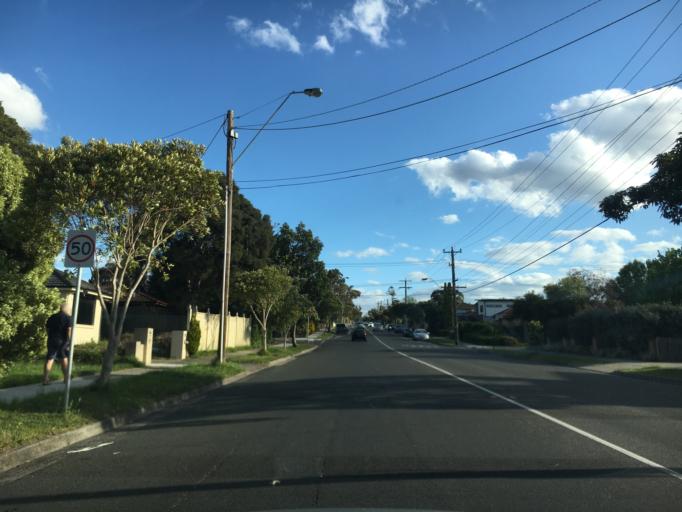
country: AU
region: Victoria
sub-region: Whitehorse
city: Vermont South
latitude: -37.8764
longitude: 145.1788
